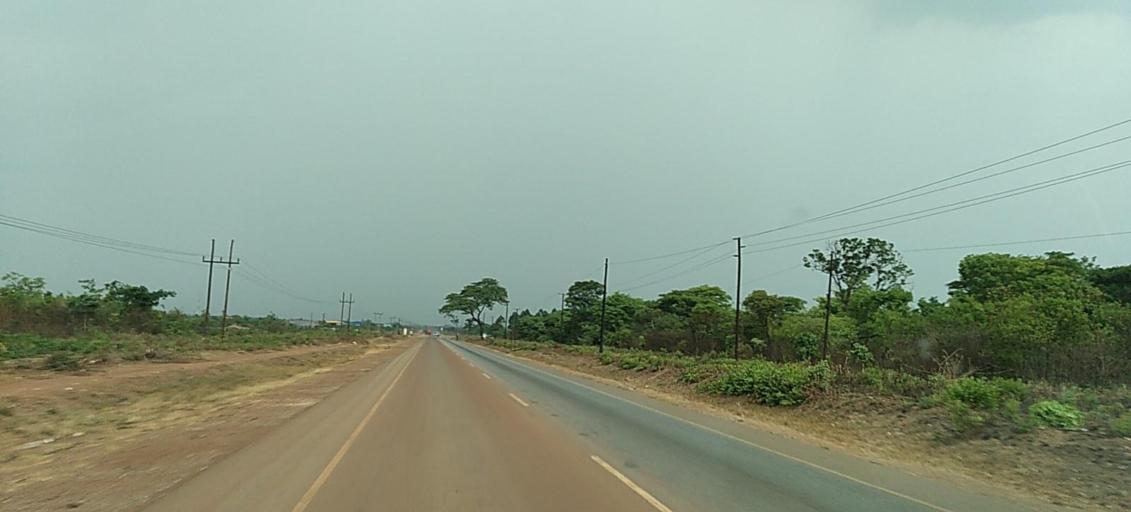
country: ZM
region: Copperbelt
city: Kalulushi
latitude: -12.8341
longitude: 28.1139
